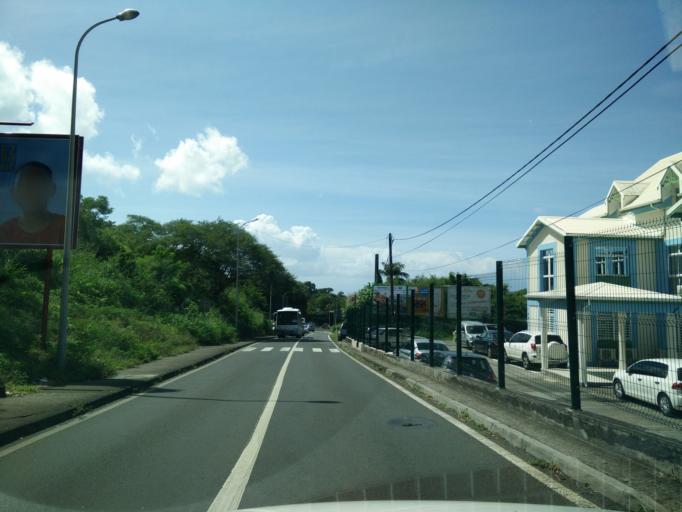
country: GP
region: Guadeloupe
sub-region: Guadeloupe
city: Basse-Terre
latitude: 16.0001
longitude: -61.7201
